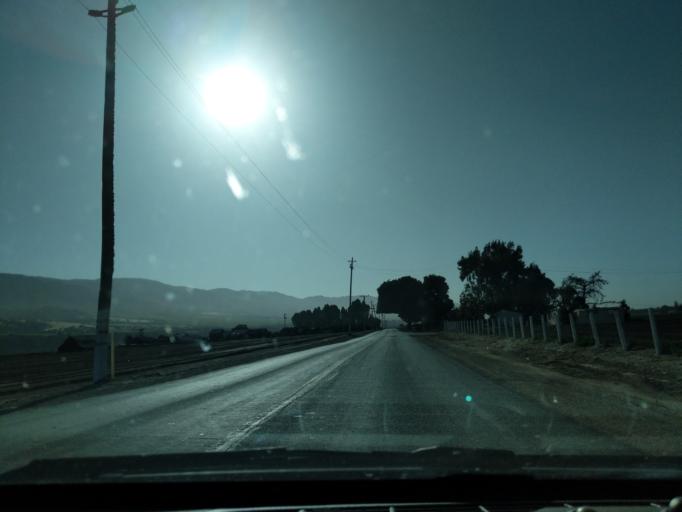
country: US
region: California
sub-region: Monterey County
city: Soledad
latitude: 36.4042
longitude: -121.3495
